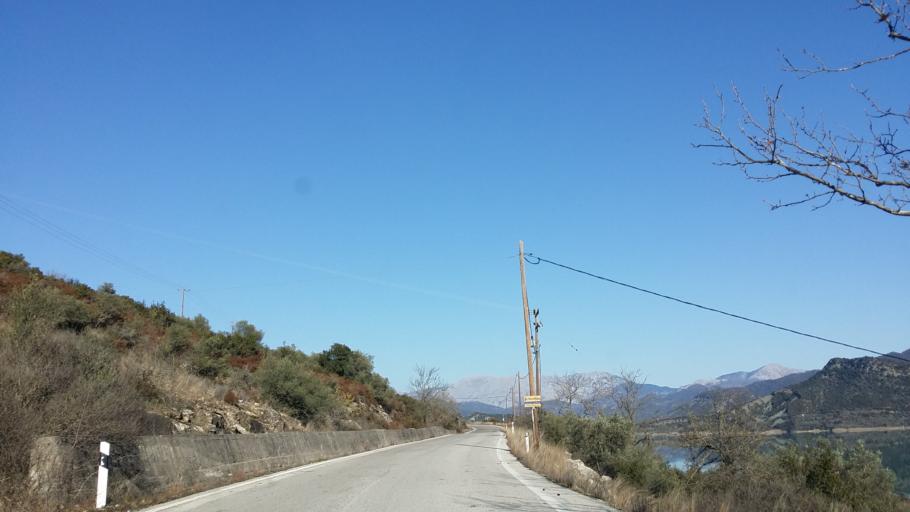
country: GR
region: West Greece
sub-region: Nomos Aitolias kai Akarnanias
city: Lepenou
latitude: 38.8160
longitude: 21.3346
